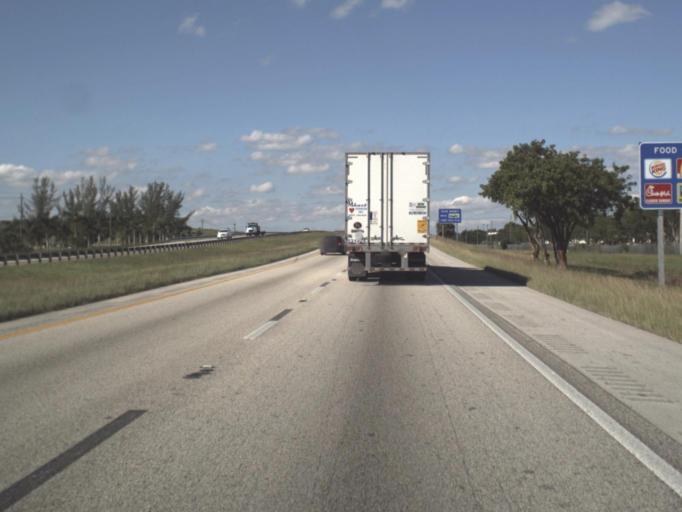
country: US
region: Florida
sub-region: Miami-Dade County
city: Lake Lucerne
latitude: 25.9717
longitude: -80.2743
